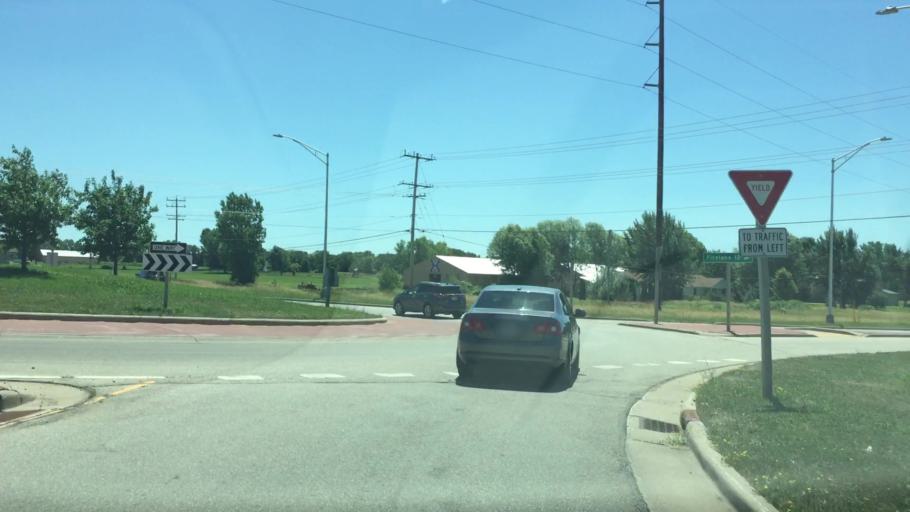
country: US
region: Wisconsin
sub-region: Outagamie County
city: Combined Locks
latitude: 44.2002
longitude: -88.3243
